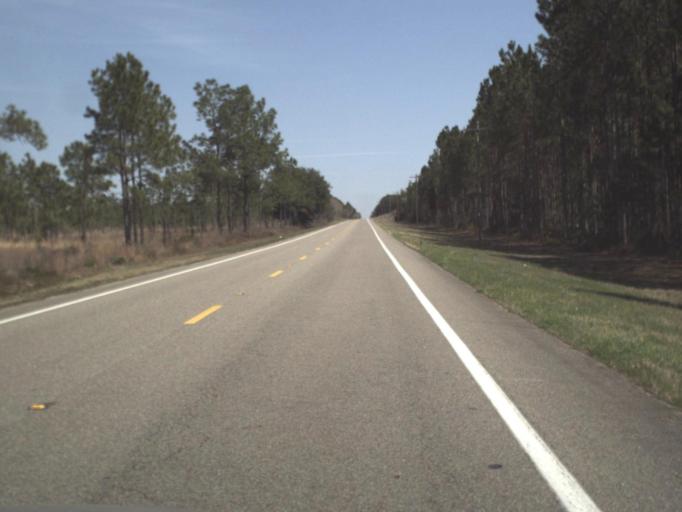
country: US
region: Florida
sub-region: Liberty County
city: Bristol
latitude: 30.4694
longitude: -84.9395
